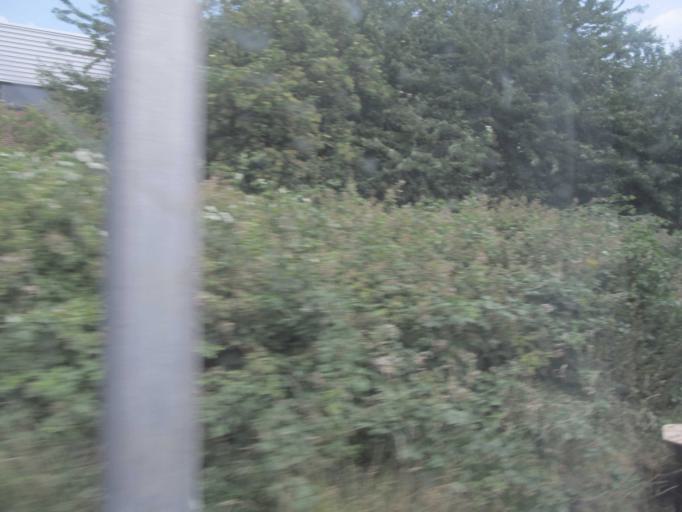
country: GB
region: England
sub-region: Buckinghamshire
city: Farnham Royal
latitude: 51.5222
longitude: -0.6362
